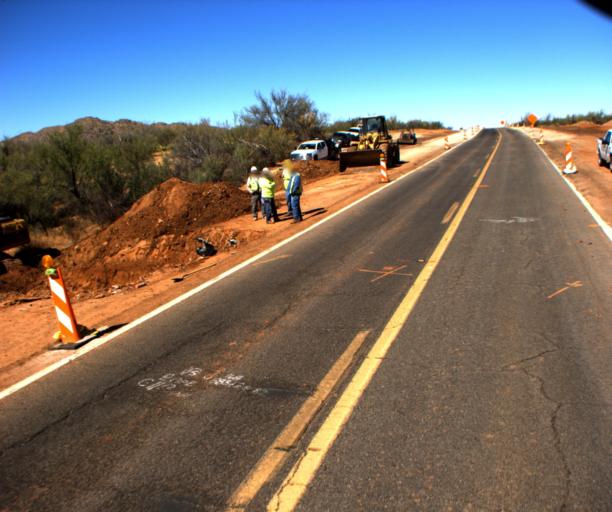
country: US
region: Arizona
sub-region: Pima County
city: Sells
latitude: 32.0070
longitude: -111.6759
